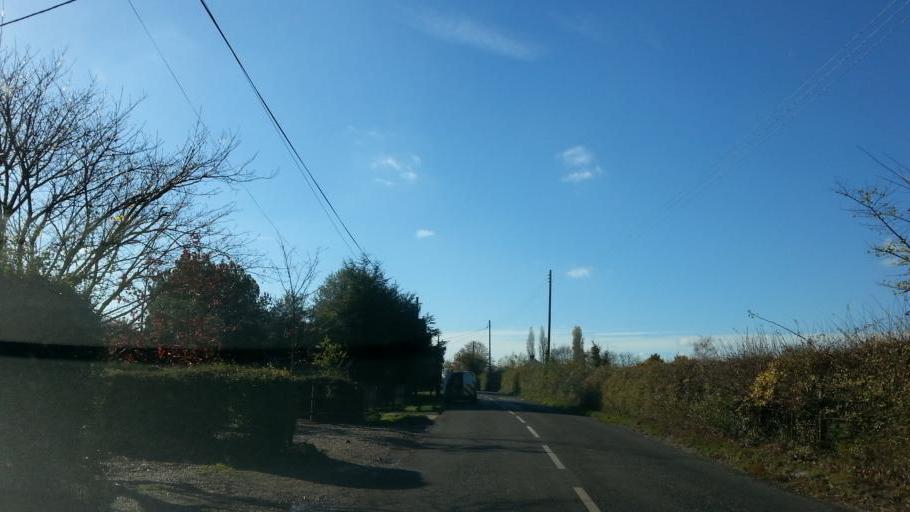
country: GB
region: England
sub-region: Suffolk
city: Cookley
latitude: 52.2961
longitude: 1.4019
